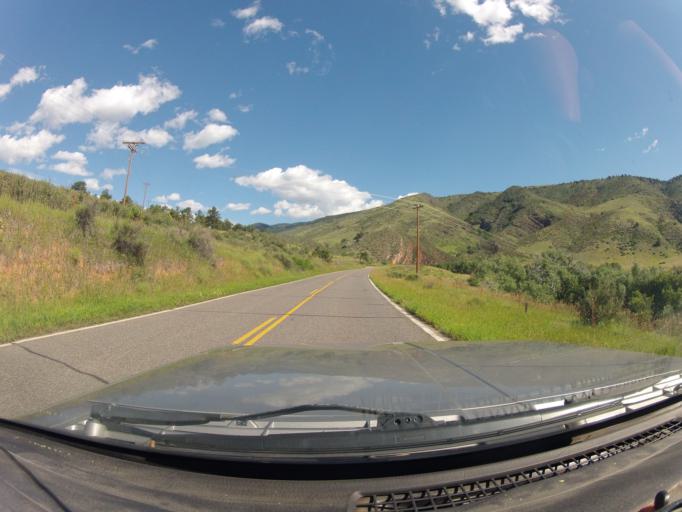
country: US
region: Colorado
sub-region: Larimer County
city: Laporte
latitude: 40.5061
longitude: -105.2290
